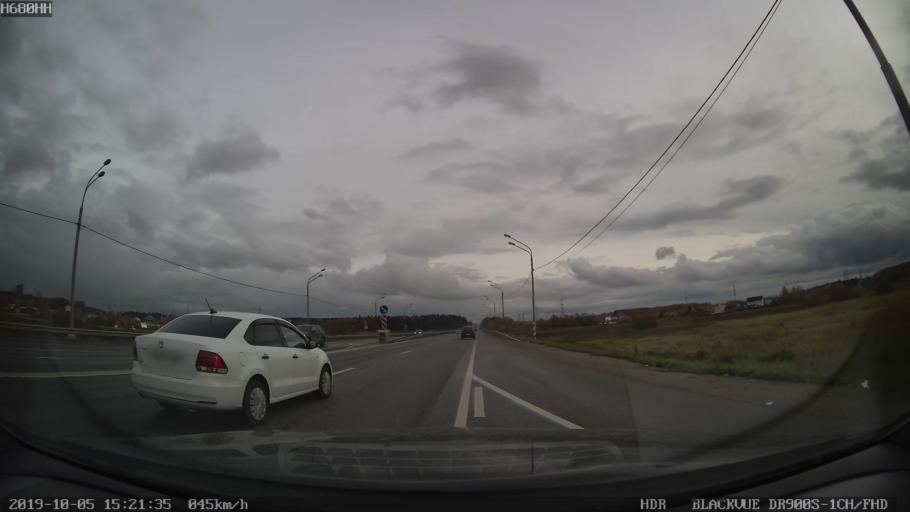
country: RU
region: Moskovskaya
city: Solnechnogorsk
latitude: 56.2275
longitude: 36.9129
